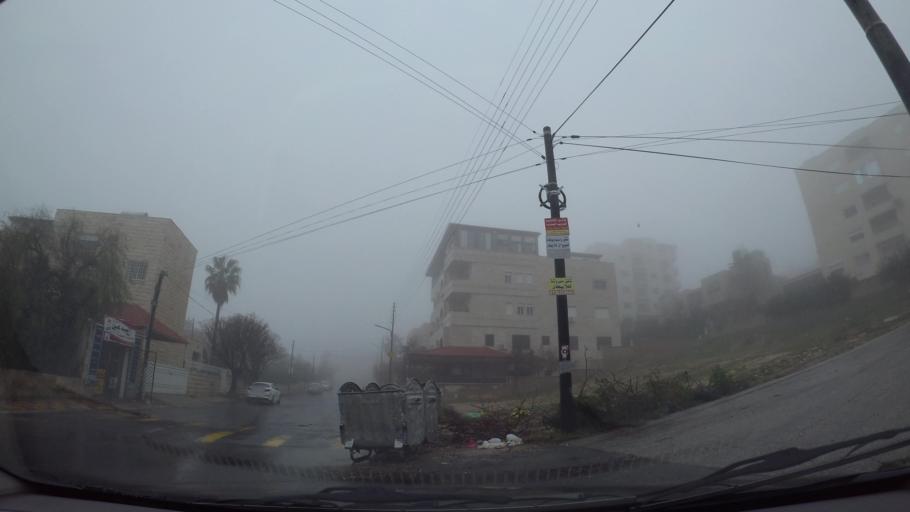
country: JO
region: Amman
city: Al Jubayhah
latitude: 32.0126
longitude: 35.8801
